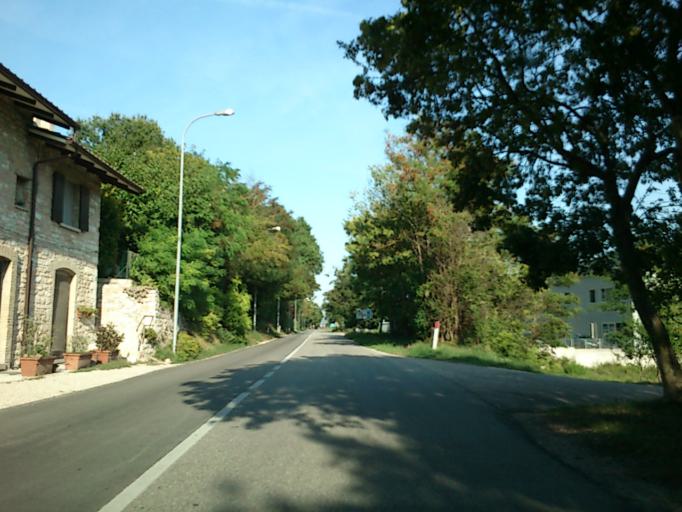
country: IT
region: The Marches
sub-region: Provincia di Pesaro e Urbino
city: Fossombrone
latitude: 43.6858
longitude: 12.7869
